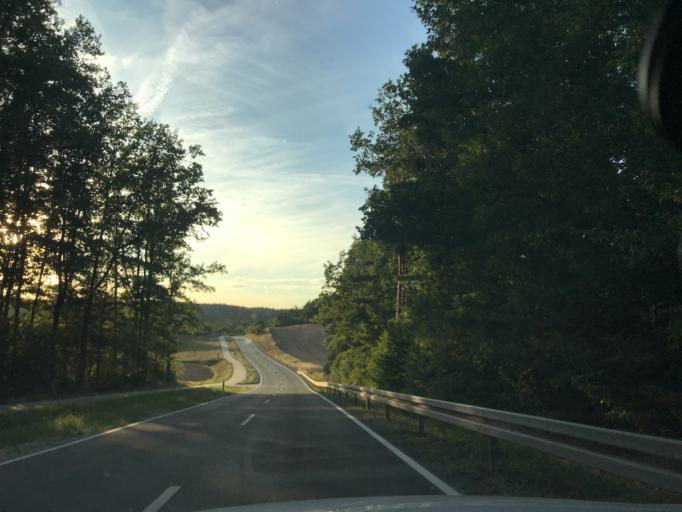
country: DE
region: Bavaria
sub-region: Upper Franconia
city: Pegnitz
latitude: 49.7198
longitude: 11.5714
